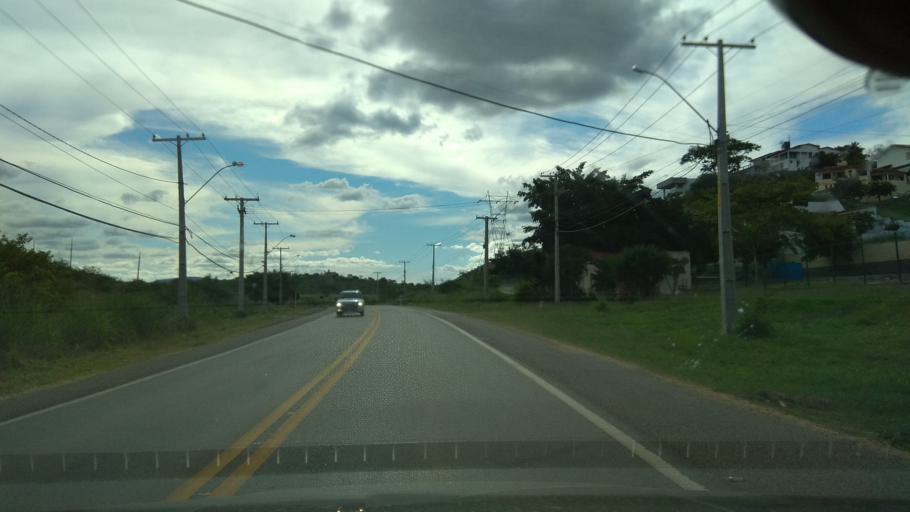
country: BR
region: Bahia
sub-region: Jequie
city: Jequie
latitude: -13.8726
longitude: -40.0420
